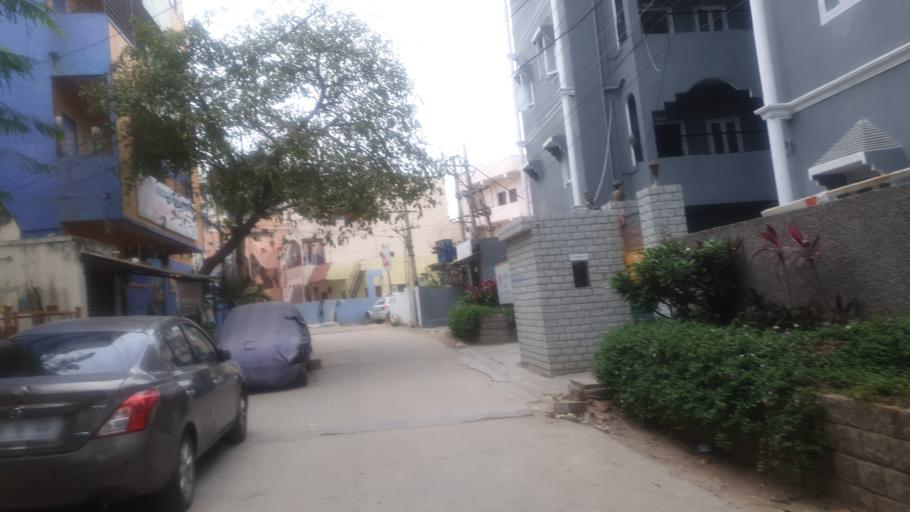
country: IN
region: Telangana
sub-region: Rangareddi
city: Kukatpalli
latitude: 17.4908
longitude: 78.3584
